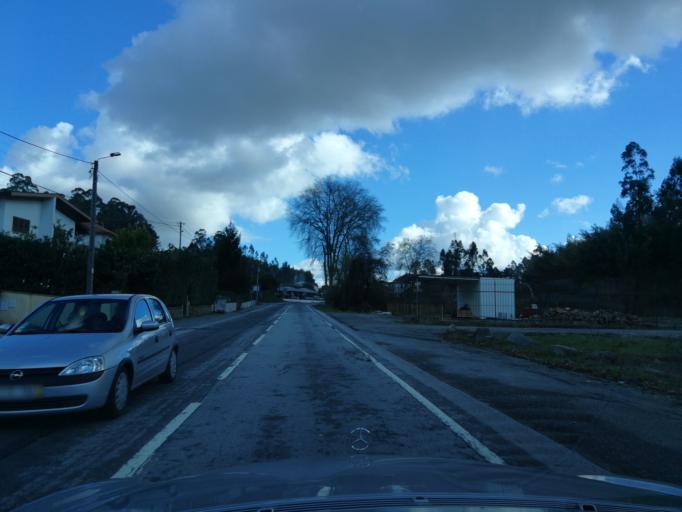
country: PT
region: Viana do Castelo
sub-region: Ponte de Lima
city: Ponte de Lima
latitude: 41.7065
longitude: -8.5388
